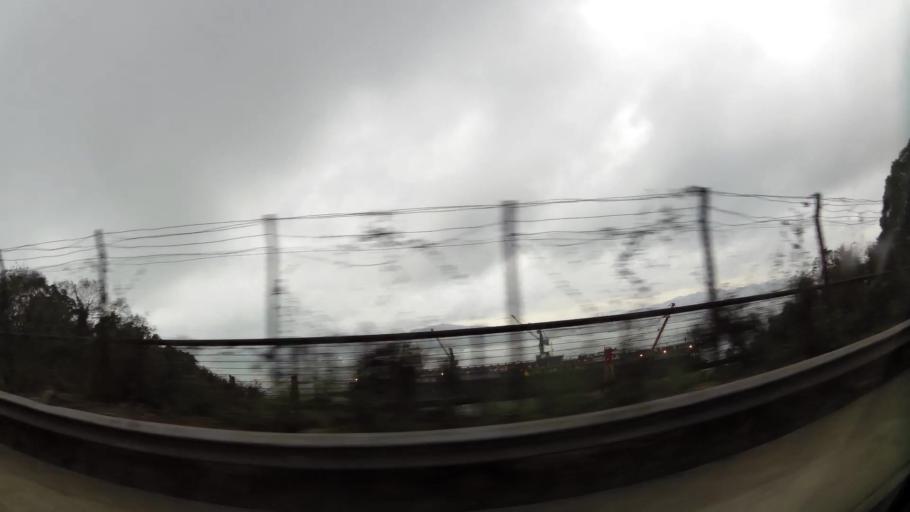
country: HK
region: Tsuen Wan
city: Tsuen Wan
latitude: 22.3333
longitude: 114.0916
